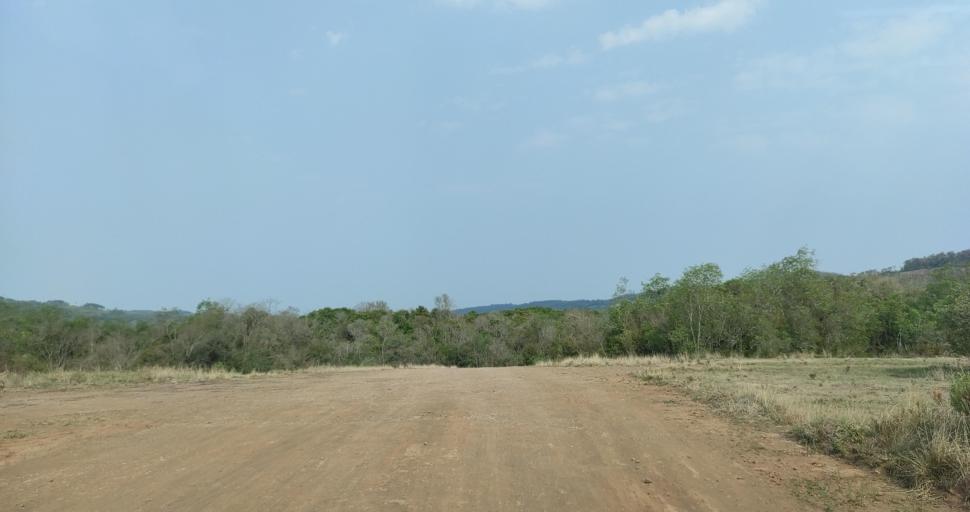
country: AR
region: Misiones
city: Cerro Cora
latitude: -27.5909
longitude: -55.5788
